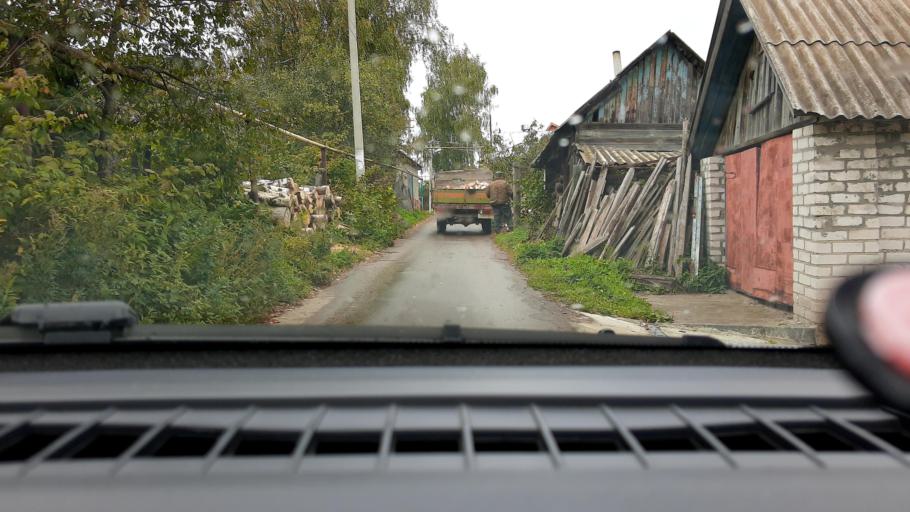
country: RU
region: Nizjnij Novgorod
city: Afonino
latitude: 56.1913
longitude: 44.0880
